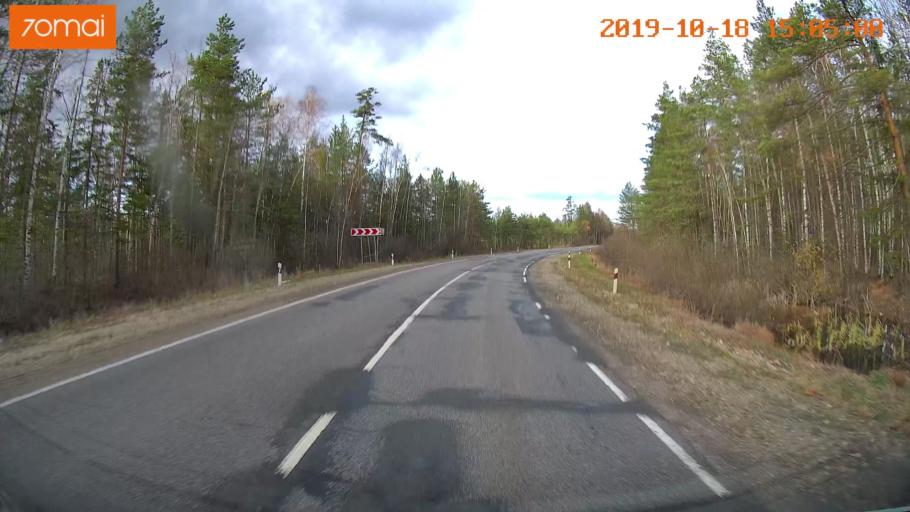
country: RU
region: Vladimir
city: Kurlovo
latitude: 55.5087
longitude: 40.5699
